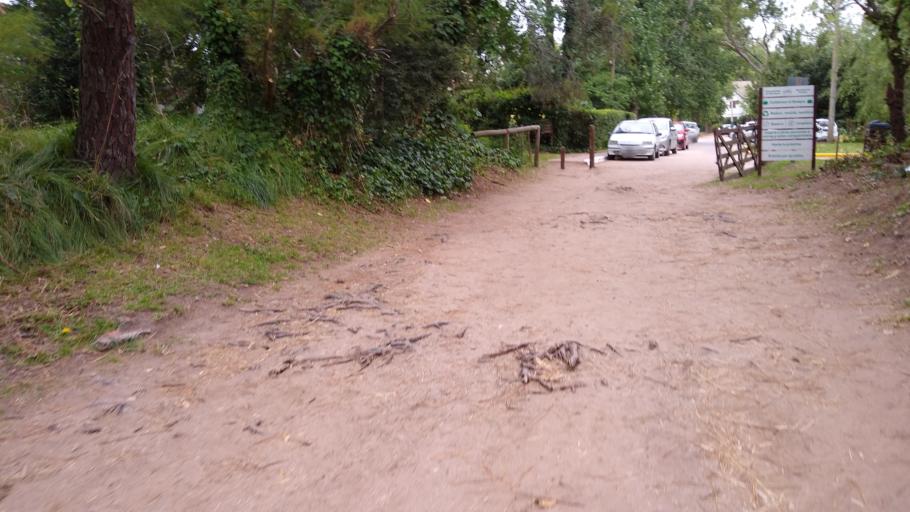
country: AR
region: Buenos Aires
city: Villa Gesell
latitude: -37.2495
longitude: -56.9647
